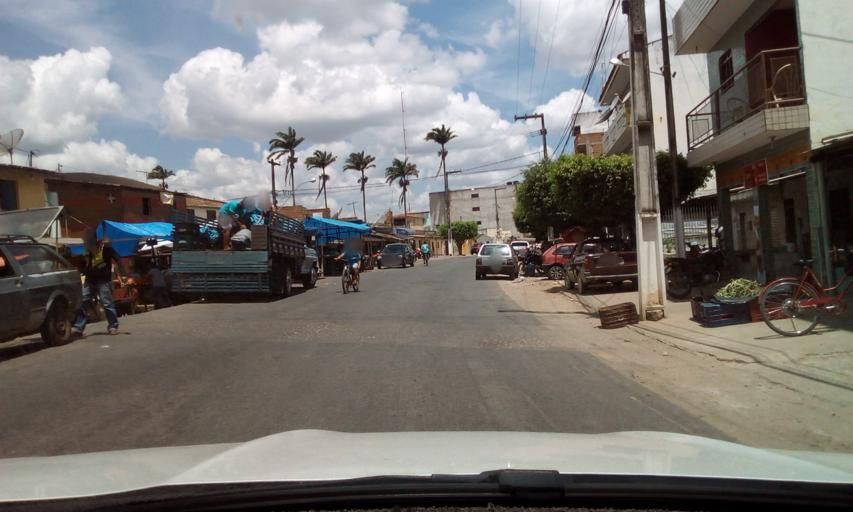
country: BR
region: Paraiba
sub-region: Alagoinha
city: Alagoinha
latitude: -6.9497
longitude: -35.5452
